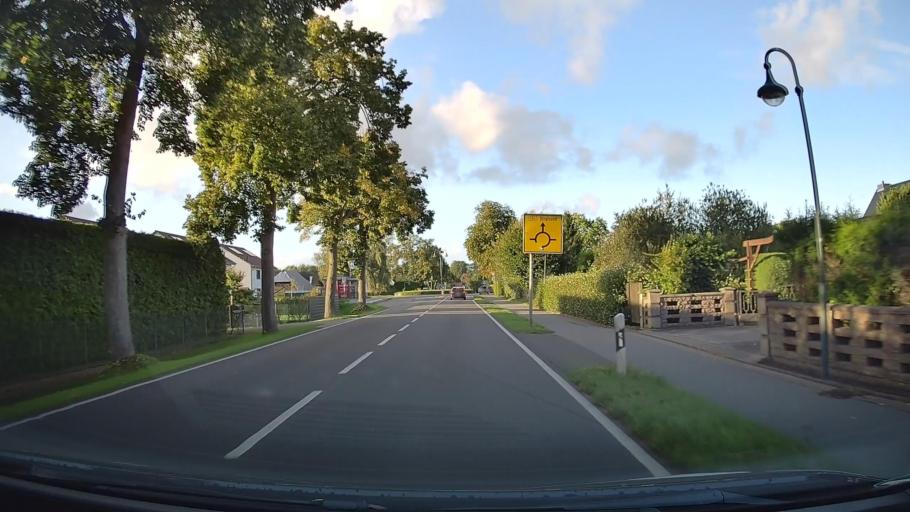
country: DE
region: Mecklenburg-Vorpommern
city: Wendorf
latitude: 54.2573
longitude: 13.0304
